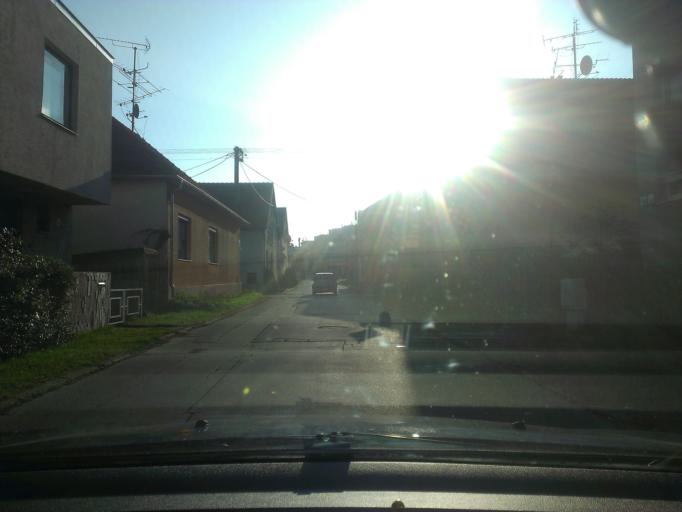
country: SK
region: Trnavsky
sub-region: Okres Trnava
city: Piestany
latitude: 48.5897
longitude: 17.8175
